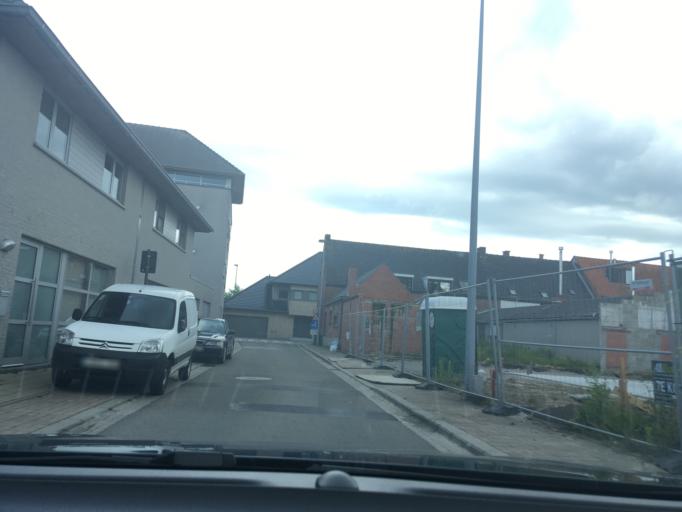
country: BE
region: Flanders
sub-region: Provincie West-Vlaanderen
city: Hooglede
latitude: 50.9415
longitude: 3.0613
